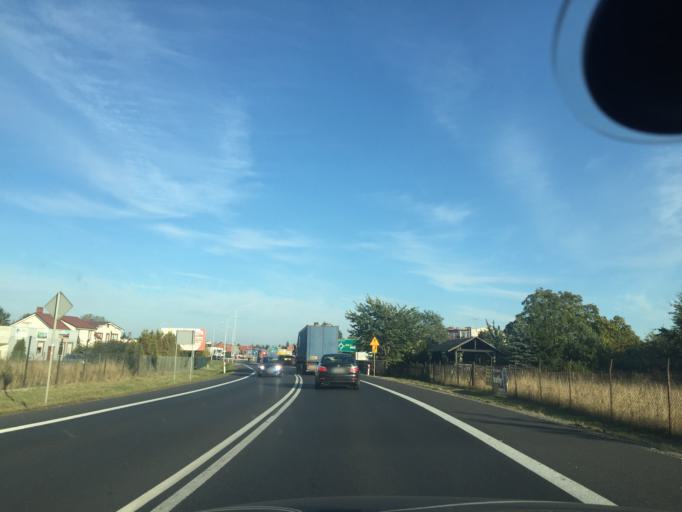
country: PL
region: Kujawsko-Pomorskie
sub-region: Powiat inowroclawski
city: Gniewkowo
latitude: 52.8973
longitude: 18.4120
